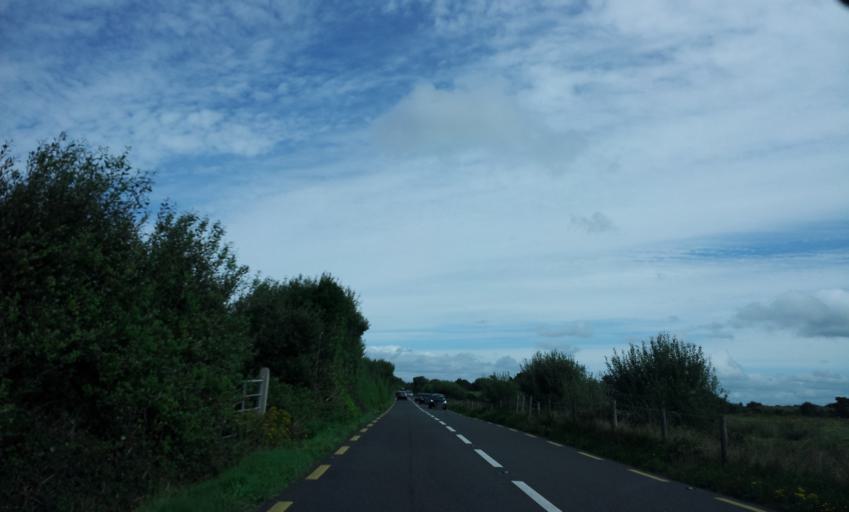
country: IE
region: Munster
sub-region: Ciarrai
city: Killorglin
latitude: 52.0820
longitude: -9.8716
